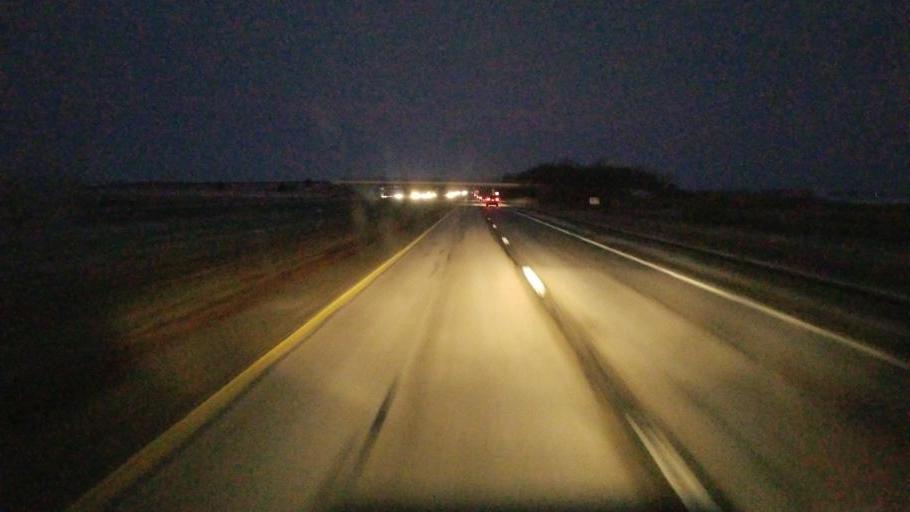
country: US
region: Ohio
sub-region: Preble County
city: Eaton
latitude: 39.8356
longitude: -84.6482
